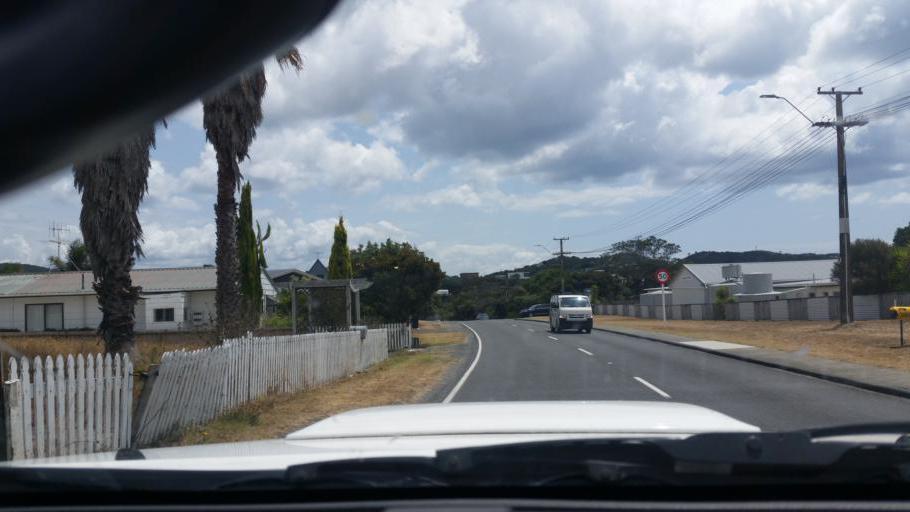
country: NZ
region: Auckland
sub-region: Auckland
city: Wellsford
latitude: -36.0920
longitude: 174.5846
